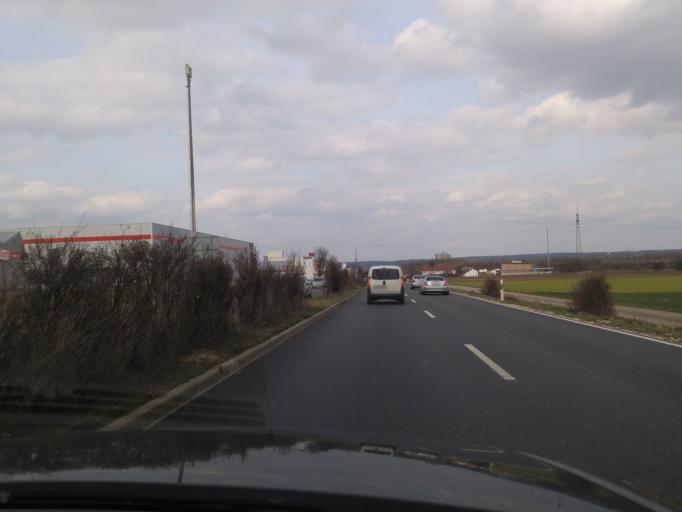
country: DE
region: Baden-Wuerttemberg
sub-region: Regierungsbezirk Stuttgart
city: Dettingen unter Teck
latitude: 48.6229
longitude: 9.4552
